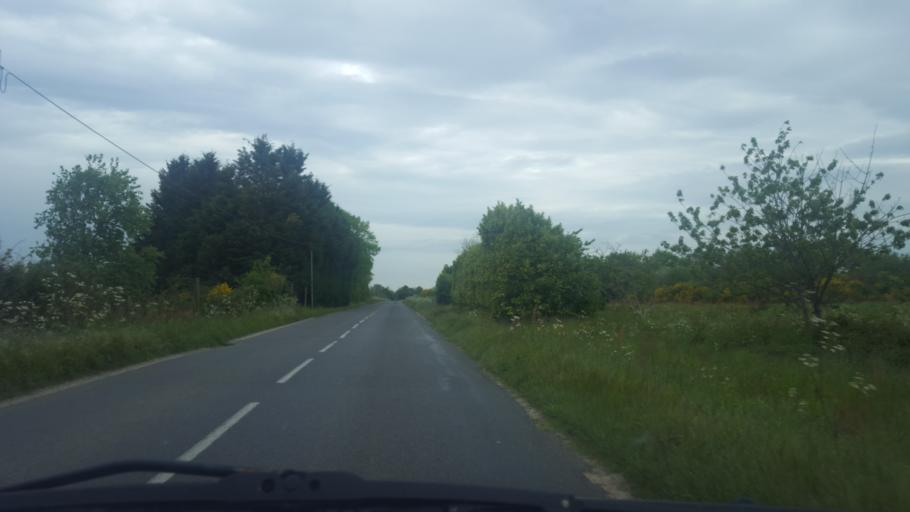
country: FR
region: Pays de la Loire
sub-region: Departement de la Loire-Atlantique
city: Geneston
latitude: 47.0440
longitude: -1.5183
